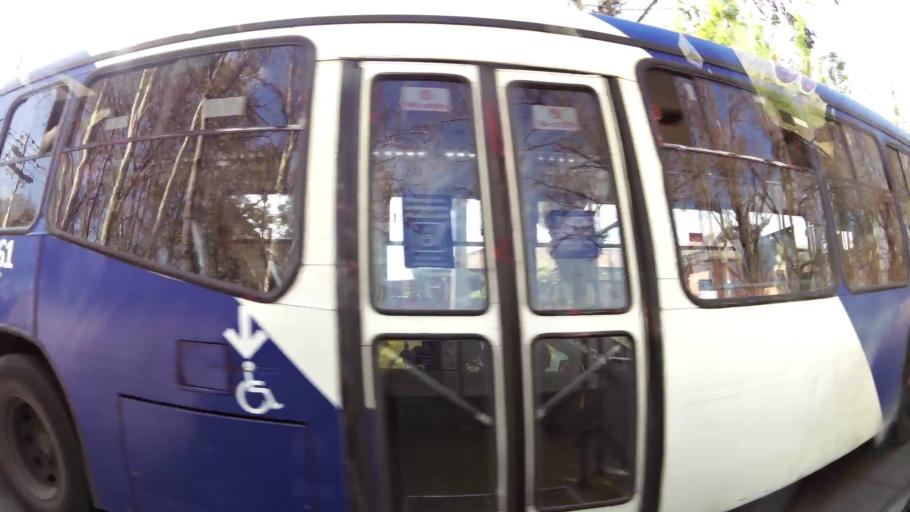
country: CL
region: Santiago Metropolitan
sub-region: Provincia de Maipo
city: San Bernardo
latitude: -33.6053
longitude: -70.7040
